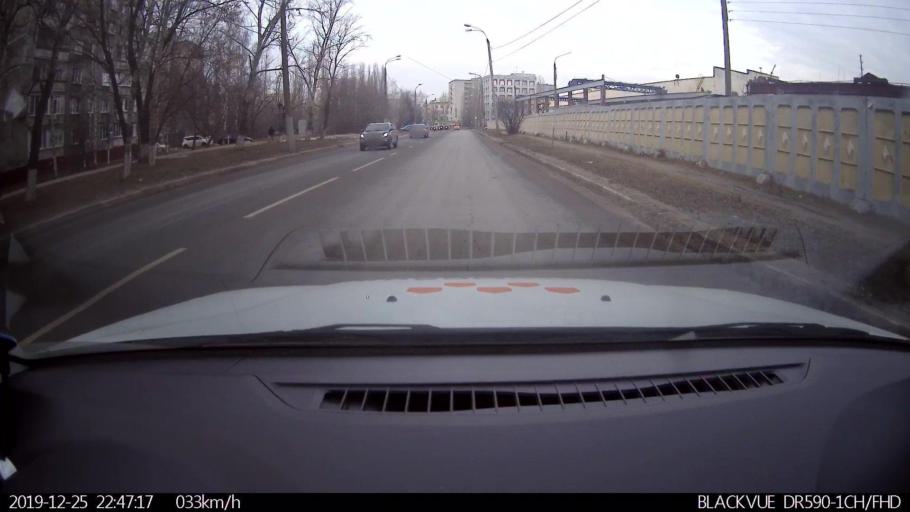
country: RU
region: Nizjnij Novgorod
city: Burevestnik
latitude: 56.2389
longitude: 43.8707
